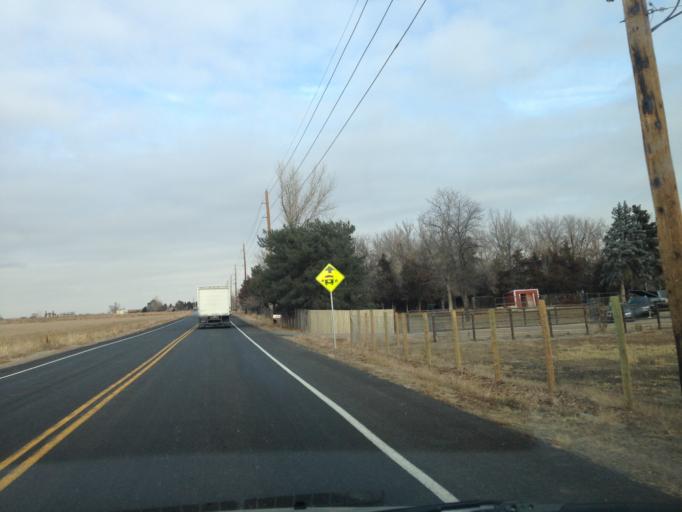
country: US
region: Colorado
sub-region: Boulder County
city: Lafayette
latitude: 40.0014
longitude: -105.0745
